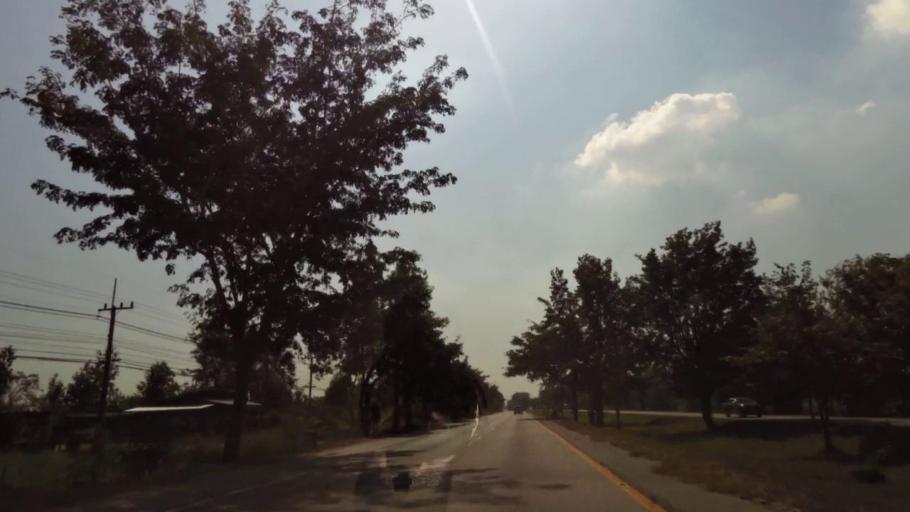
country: TH
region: Phichit
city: Wachira Barami
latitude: 16.5384
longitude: 100.1445
